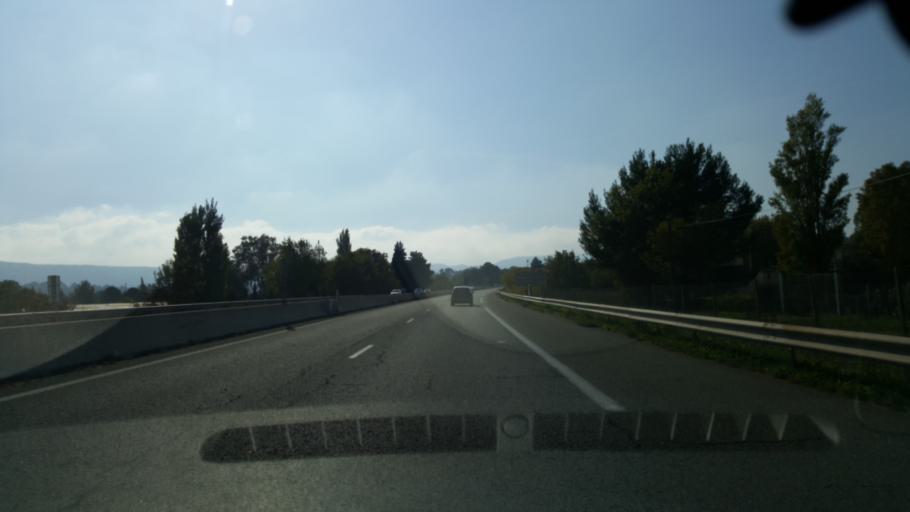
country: FR
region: Provence-Alpes-Cote d'Azur
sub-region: Departement des Bouches-du-Rhone
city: Aubagne
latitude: 43.3105
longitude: 5.5810
